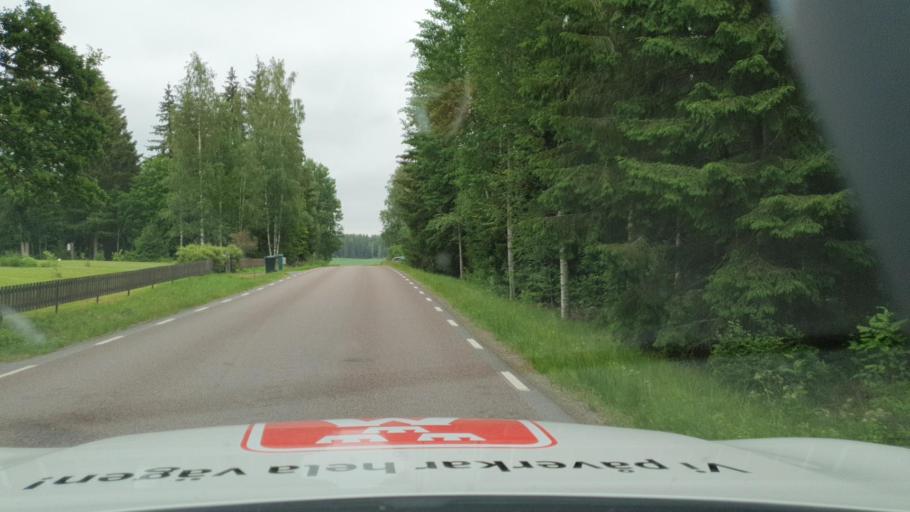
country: SE
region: Vaermland
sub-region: Kristinehamns Kommun
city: Kristinehamn
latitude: 59.4284
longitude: 13.9173
